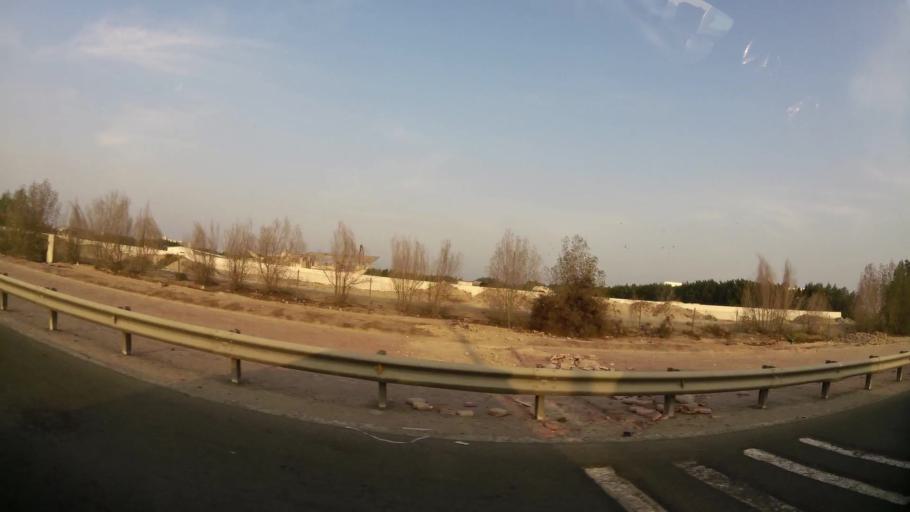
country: KW
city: Al Funaytis
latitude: 29.2548
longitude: 48.0898
